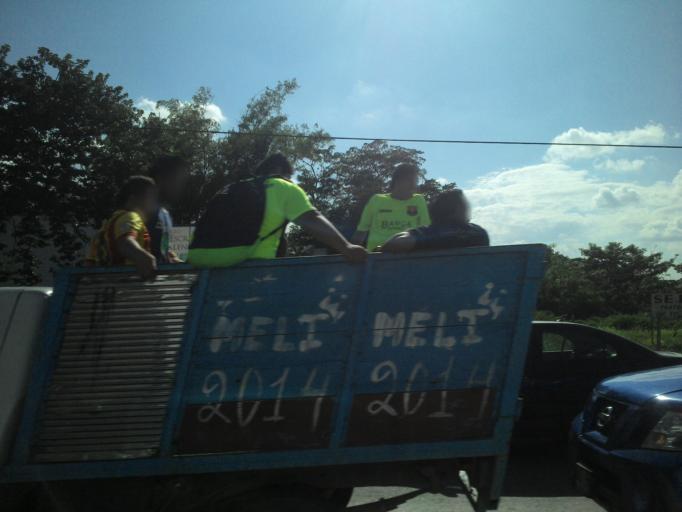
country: MX
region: Chiapas
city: Palenque
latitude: 17.5141
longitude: -91.9924
